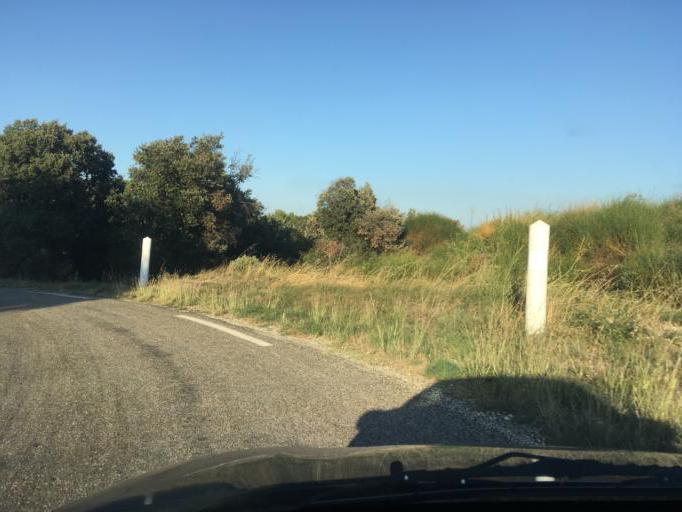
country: FR
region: Languedoc-Roussillon
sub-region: Departement du Gard
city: Tavel
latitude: 44.0136
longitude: 4.6571
